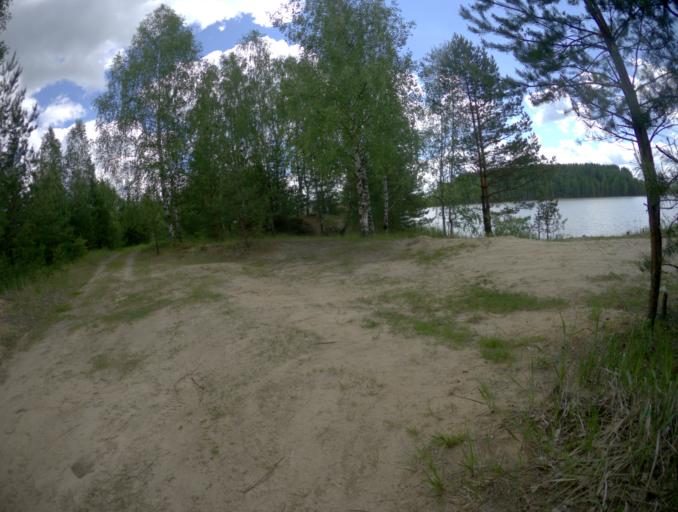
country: RU
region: Vladimir
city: Velikodvorskiy
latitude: 55.2343
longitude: 40.6352
